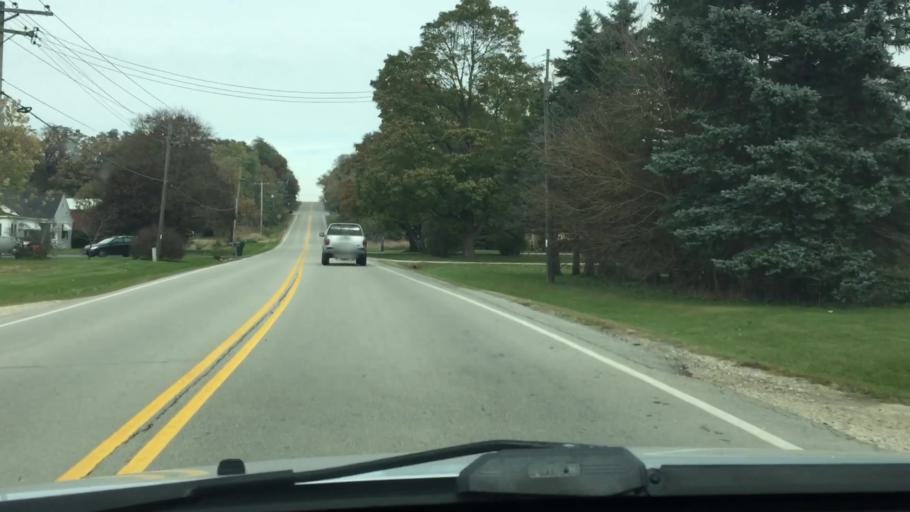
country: US
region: Wisconsin
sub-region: Waukesha County
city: North Prairie
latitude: 42.9200
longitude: -88.4054
